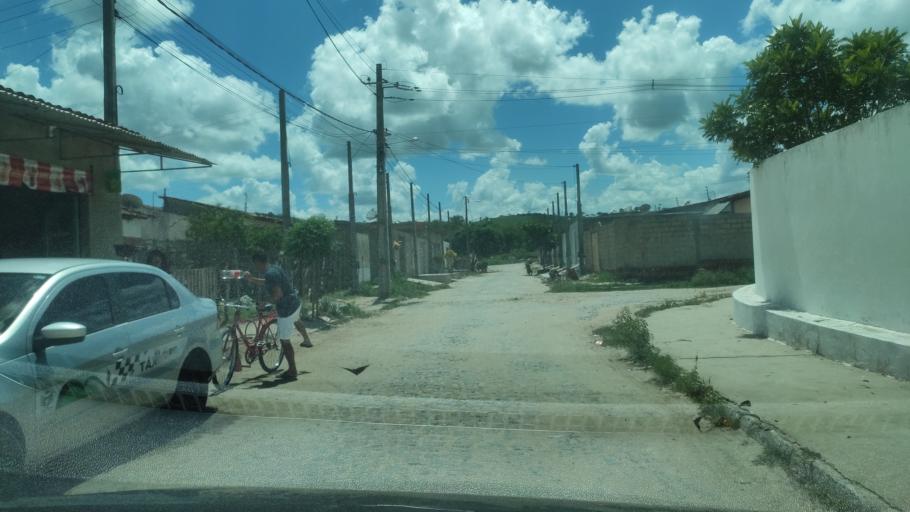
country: BR
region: Alagoas
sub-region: Uniao Dos Palmares
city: Uniao dos Palmares
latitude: -9.1458
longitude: -36.0024
